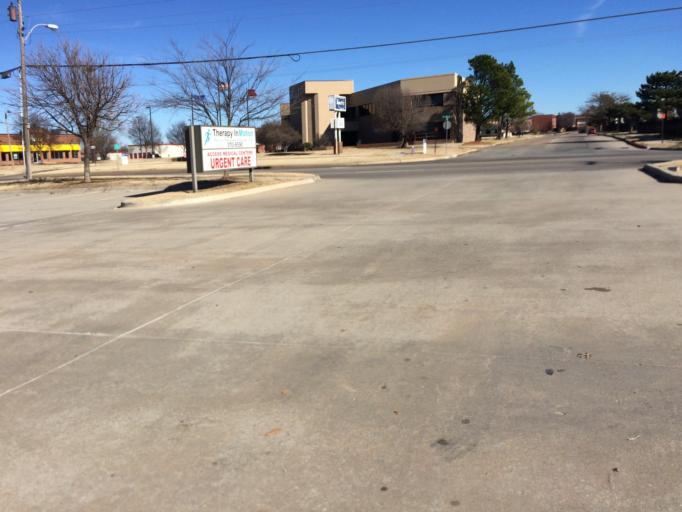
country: US
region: Oklahoma
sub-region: Cleveland County
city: Norman
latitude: 35.2141
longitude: -97.4240
